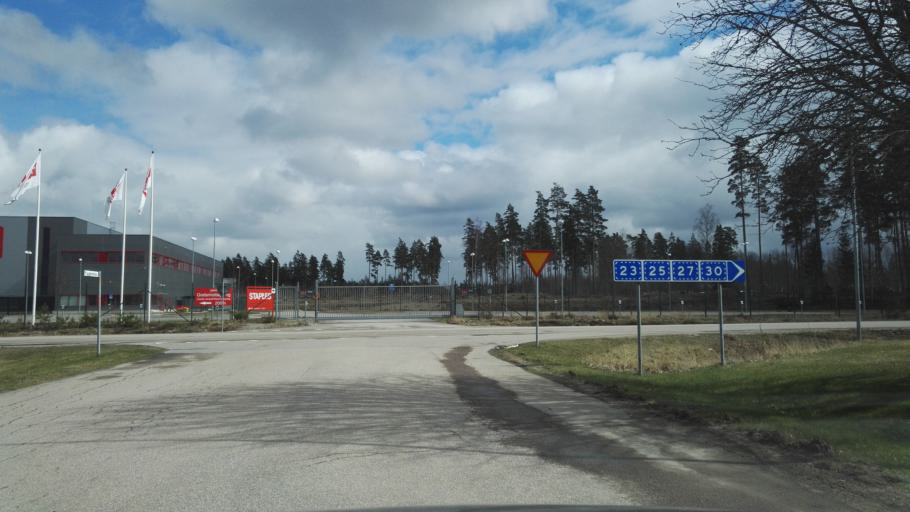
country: SE
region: Kronoberg
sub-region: Vaxjo Kommun
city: Vaexjoe
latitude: 56.9241
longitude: 14.7337
